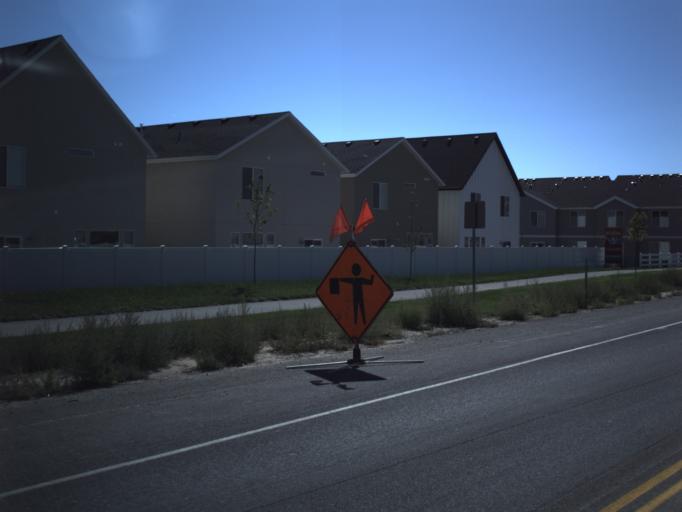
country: US
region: Utah
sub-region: Utah County
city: Saratoga Springs
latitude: 40.3538
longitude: -111.9163
